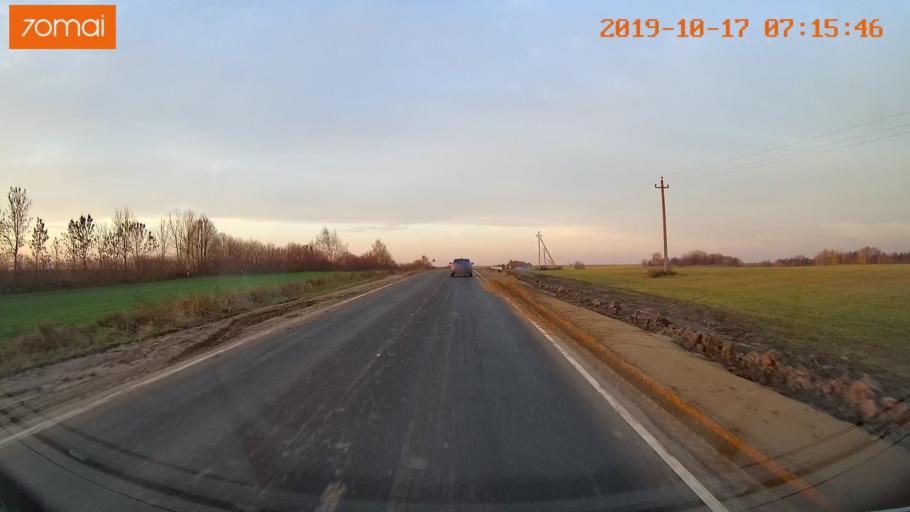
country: RU
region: Vladimir
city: Suzdal'
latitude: 56.3776
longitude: 40.2620
